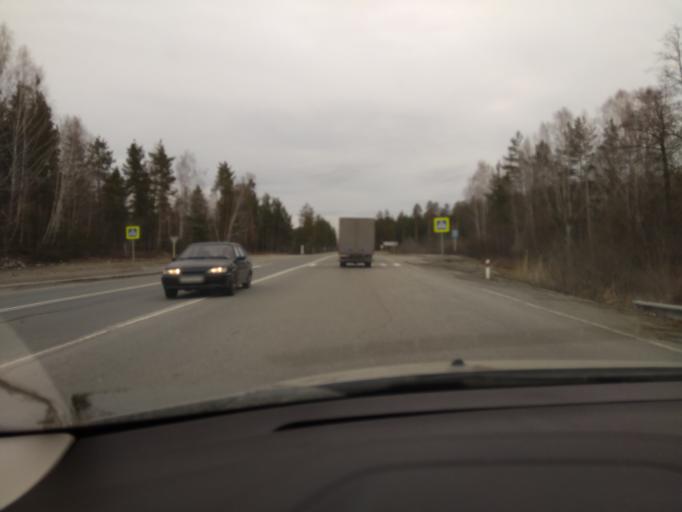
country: RU
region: Chelyabinsk
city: Kyshtym
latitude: 55.6922
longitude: 60.5001
